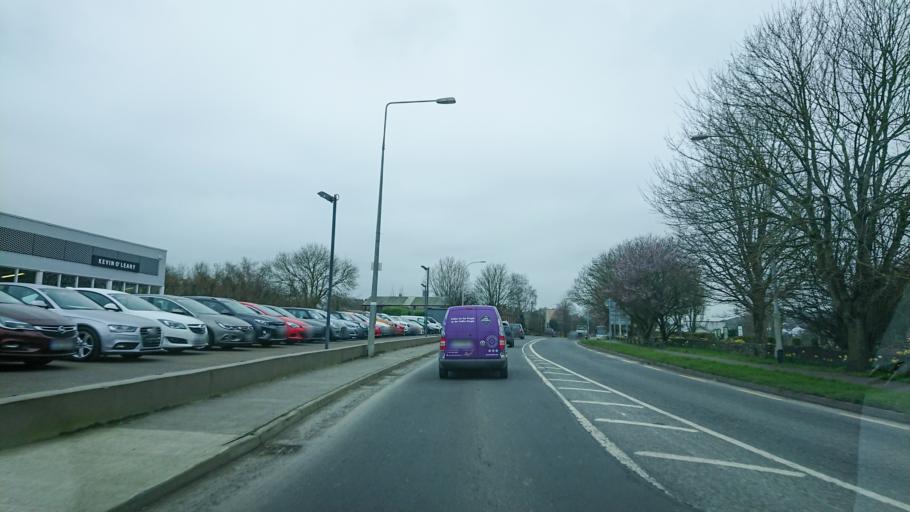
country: IE
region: Munster
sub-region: County Cork
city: Bandon
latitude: 51.7469
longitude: -8.7262
